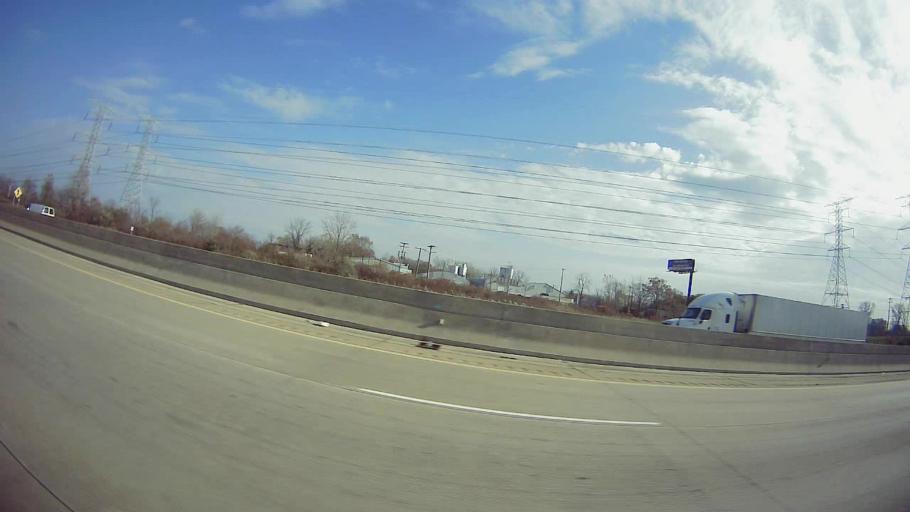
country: US
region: Michigan
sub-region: Monroe County
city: South Rockwood
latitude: 42.0643
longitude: -83.2574
